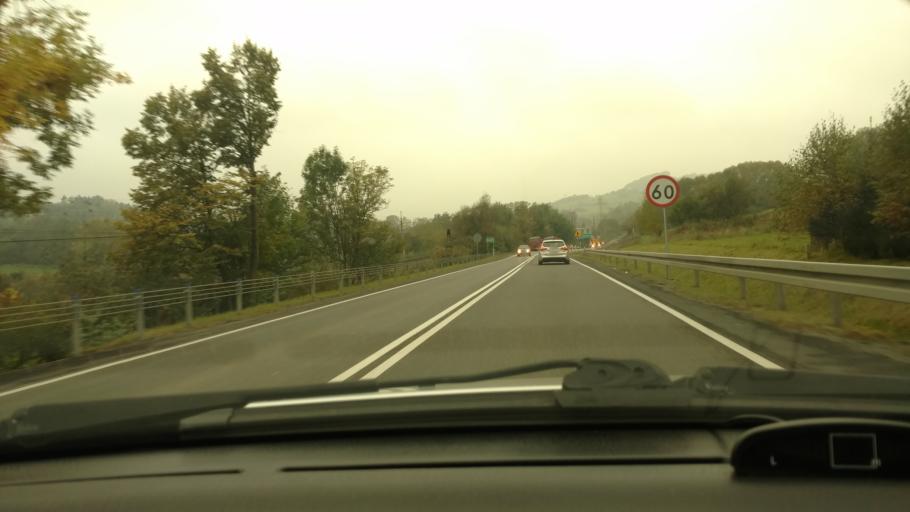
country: PL
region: Lesser Poland Voivodeship
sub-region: Powiat nowosadecki
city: Grybow
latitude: 49.6240
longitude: 20.9210
